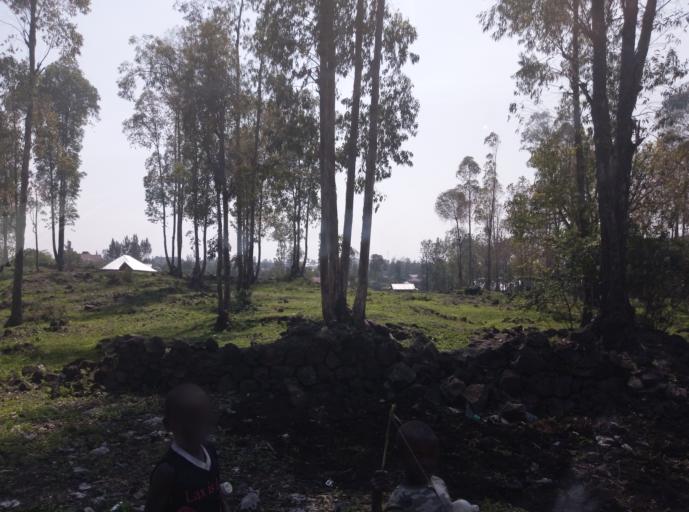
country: CD
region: Nord Kivu
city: Goma
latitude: -1.6396
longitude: 29.1693
